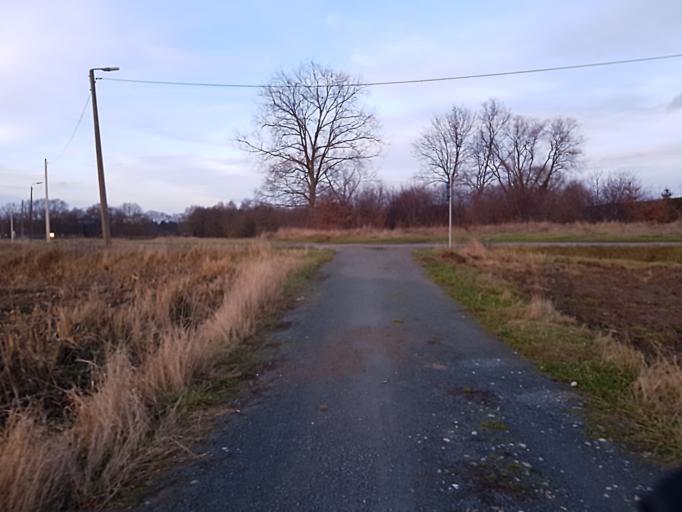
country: BE
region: Flanders
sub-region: Provincie Vlaams-Brabant
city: Tremelo
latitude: 50.9831
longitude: 4.6812
